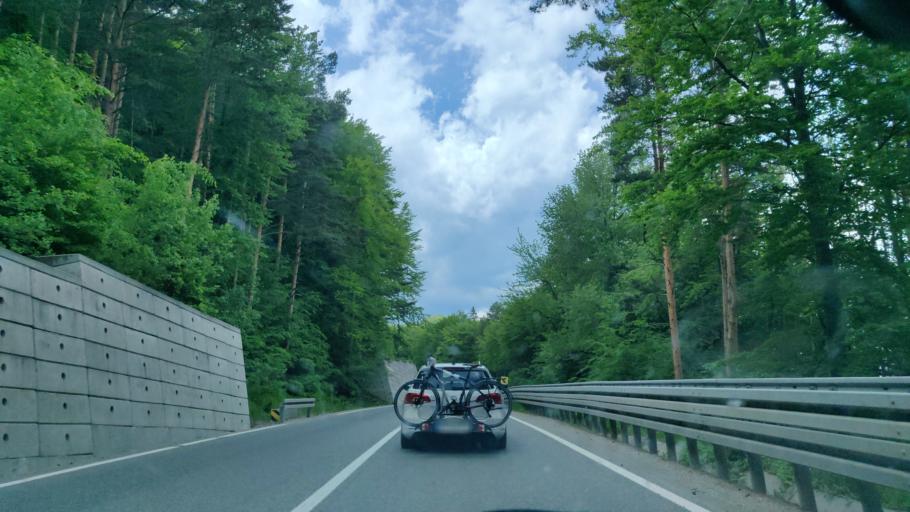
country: RO
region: Vrancea
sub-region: Comuna Tulnici
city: Tulnici
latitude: 45.9183
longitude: 26.6634
